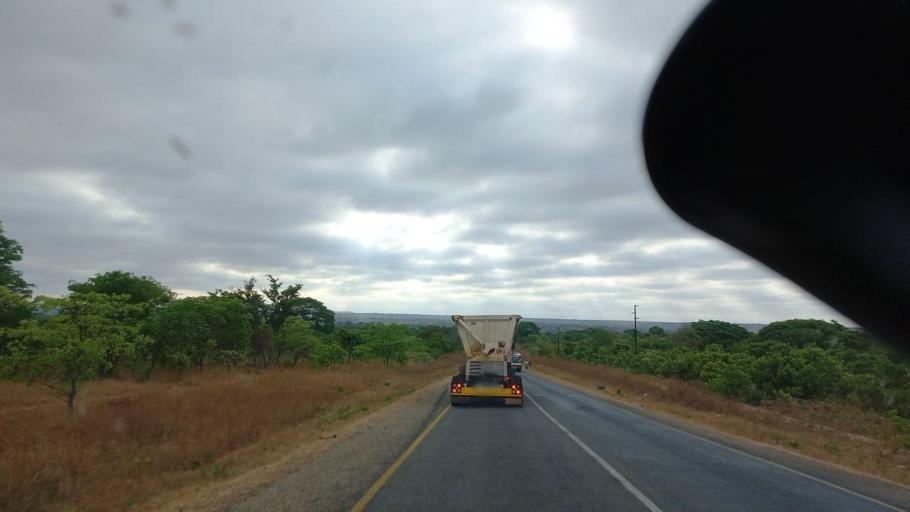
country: ZM
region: Lusaka
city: Chongwe
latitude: -15.2809
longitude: 28.7851
